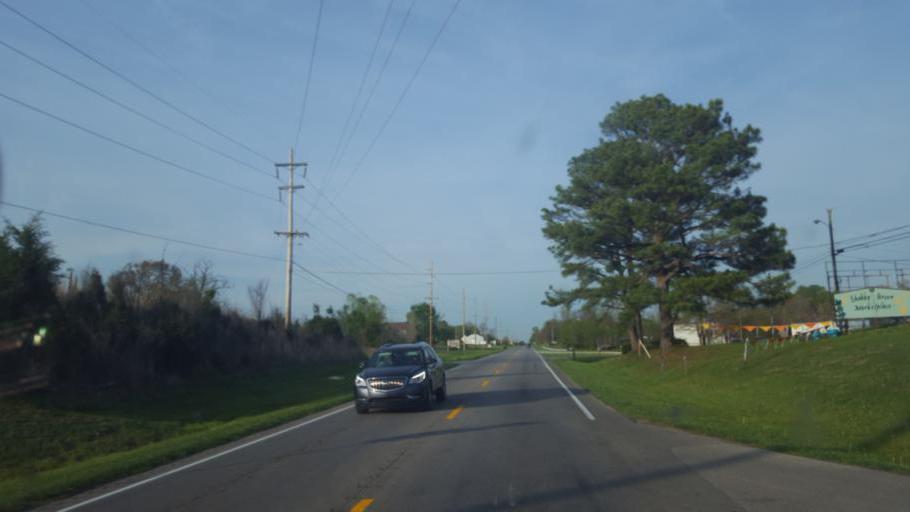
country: US
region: Kentucky
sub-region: Barren County
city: Glasgow
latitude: 36.9528
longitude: -85.9638
